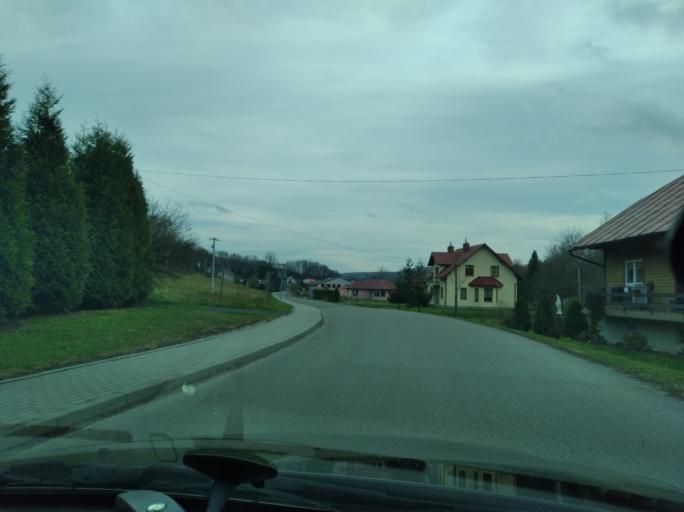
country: PL
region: Subcarpathian Voivodeship
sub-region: Powiat strzyzowski
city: Strzyzow
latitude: 49.9326
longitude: 21.7659
